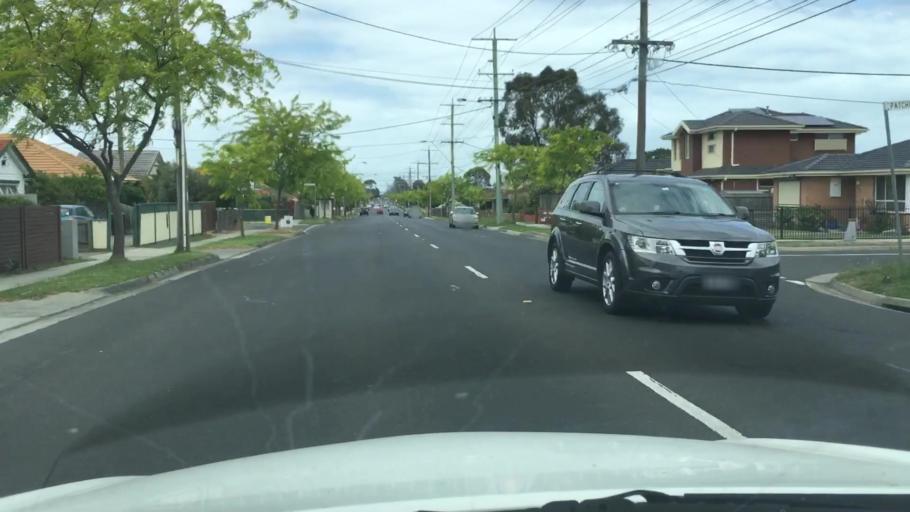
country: AU
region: Victoria
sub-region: Greater Dandenong
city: Noble Park
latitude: -37.9748
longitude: 145.1665
